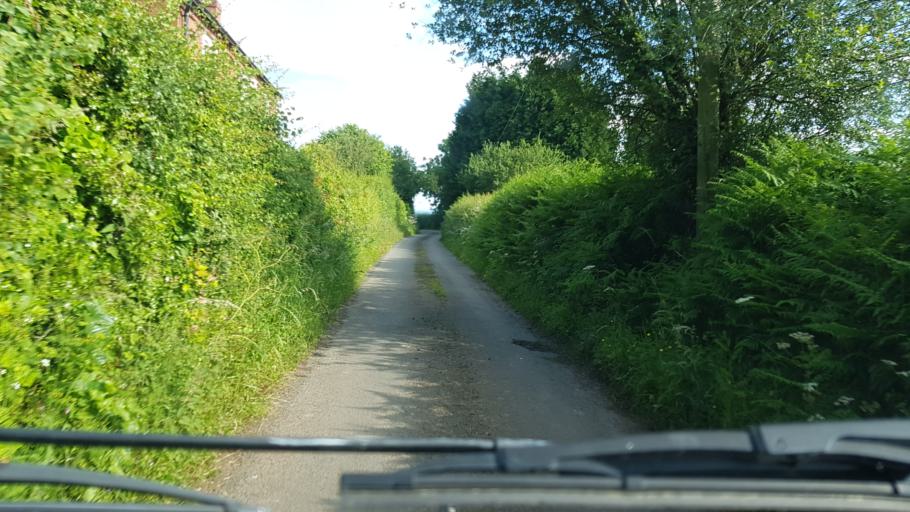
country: GB
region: England
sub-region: Worcestershire
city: Bewdley
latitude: 52.3349
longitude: -2.3194
